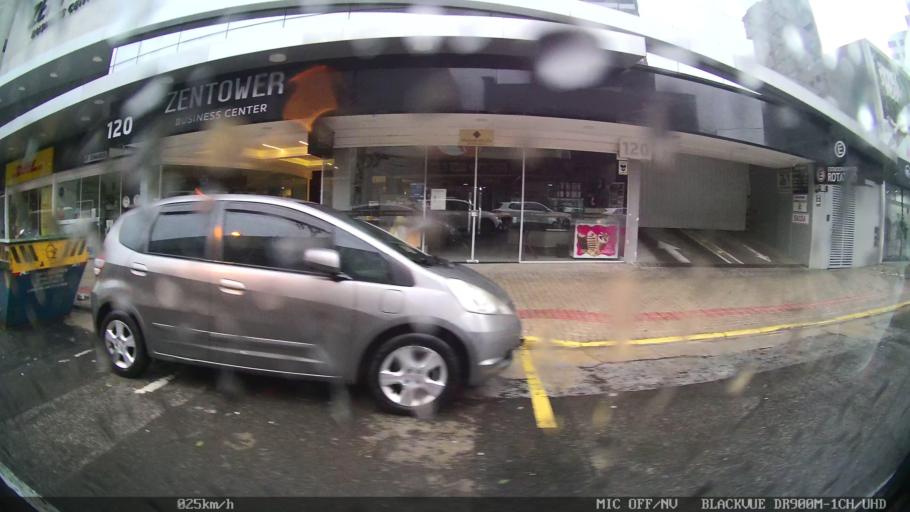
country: BR
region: Santa Catarina
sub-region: Itajai
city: Itajai
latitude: -26.9050
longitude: -48.6570
